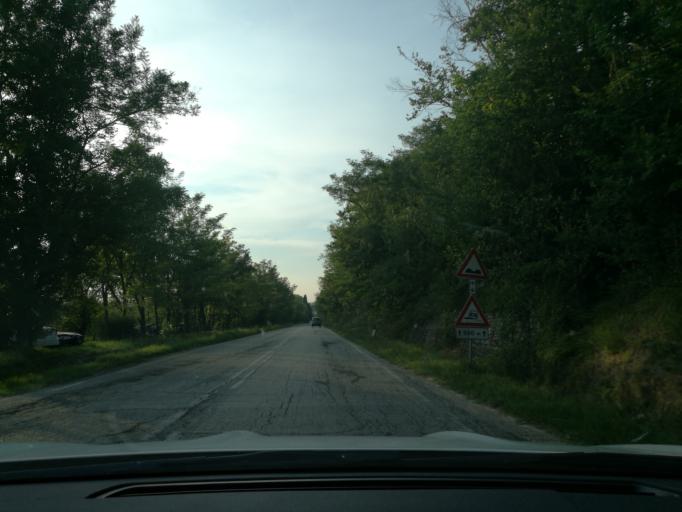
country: IT
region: Umbria
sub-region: Provincia di Terni
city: San Gemini
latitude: 42.6353
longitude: 12.5491
